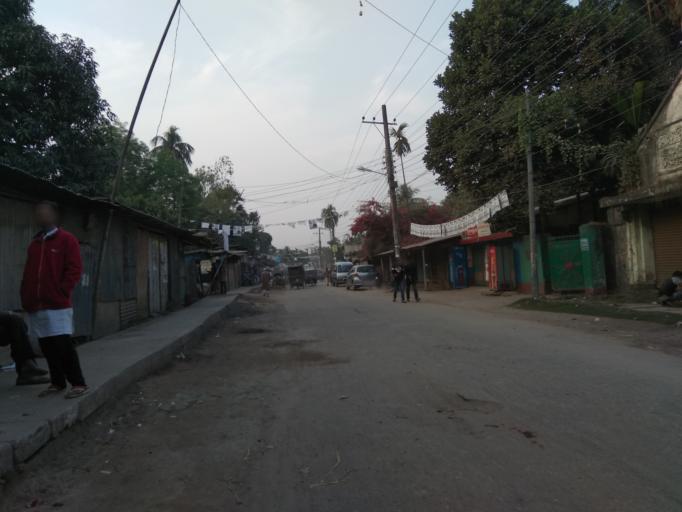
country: BD
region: Rangpur Division
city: Rangpur
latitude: 25.7303
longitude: 89.2630
